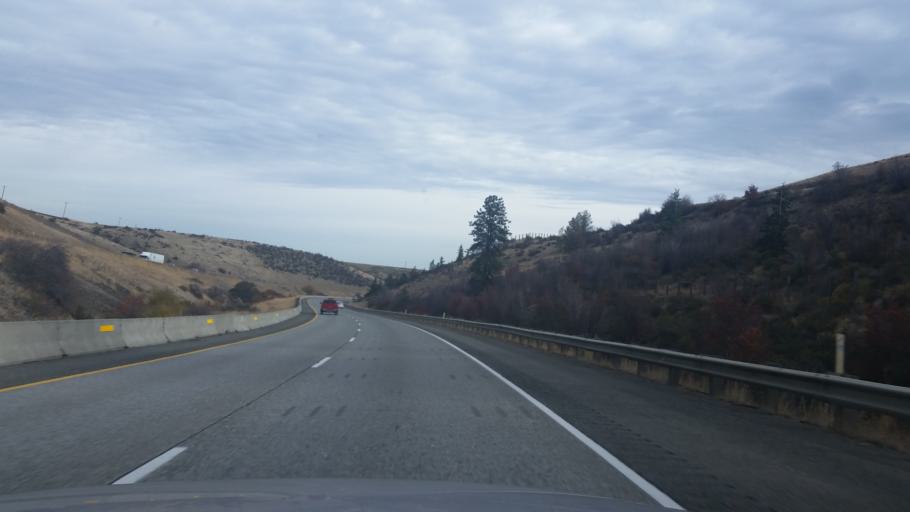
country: US
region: Washington
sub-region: Kittitas County
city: Cle Elum
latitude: 47.0924
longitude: -120.7535
